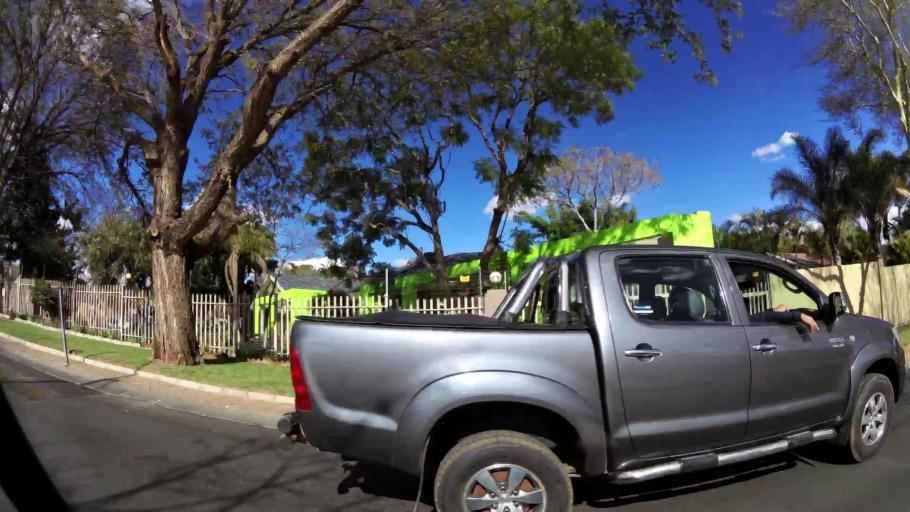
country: ZA
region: Limpopo
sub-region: Capricorn District Municipality
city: Polokwane
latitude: -23.8900
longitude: 29.4776
